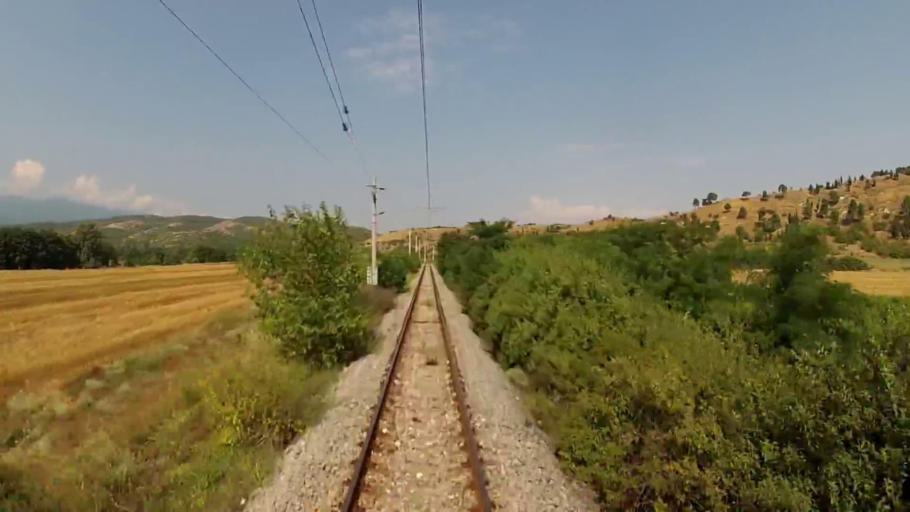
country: BG
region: Blagoevgrad
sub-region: Obshtina Petrich
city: Petrich
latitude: 41.4256
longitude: 23.3289
